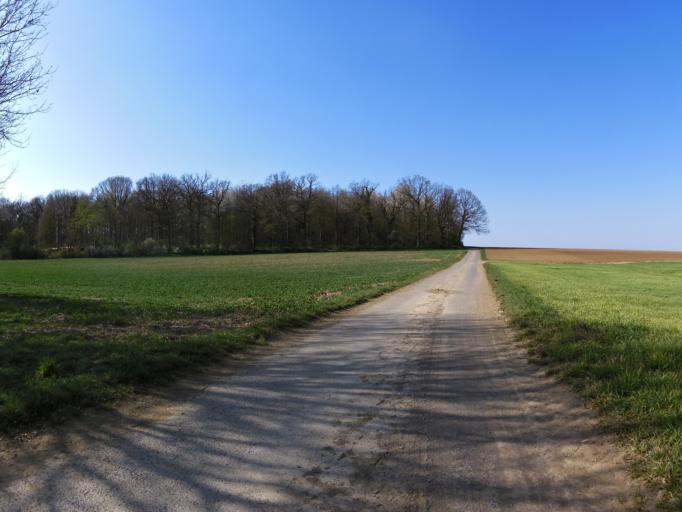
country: DE
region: Bavaria
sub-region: Regierungsbezirk Unterfranken
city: Kurnach
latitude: 49.8286
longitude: 10.0775
